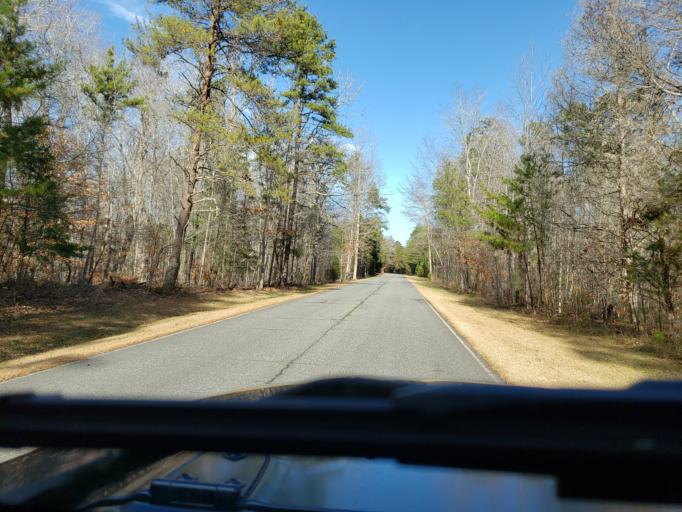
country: US
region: North Carolina
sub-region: Cleveland County
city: White Plains
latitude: 35.1368
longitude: -81.3532
